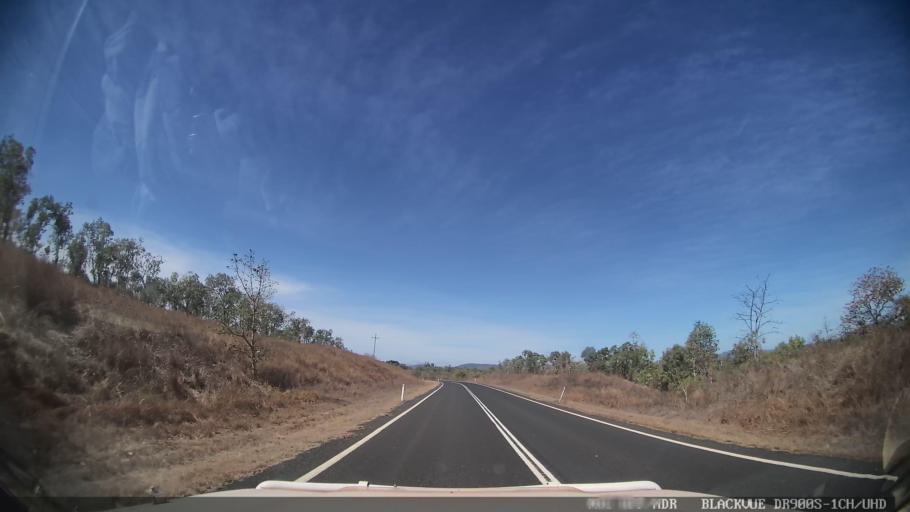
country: AU
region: Queensland
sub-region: Cook
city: Cooktown
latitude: -15.8656
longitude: 144.8153
